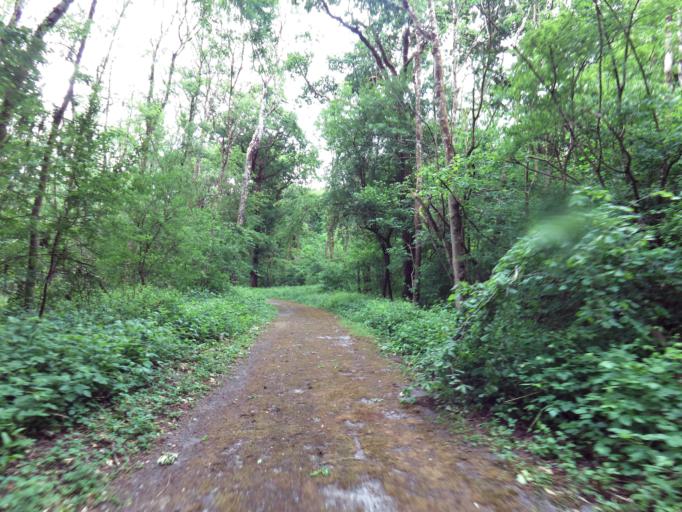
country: IE
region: Connaught
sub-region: County Galway
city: Gort
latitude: 53.0778
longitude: -8.8692
